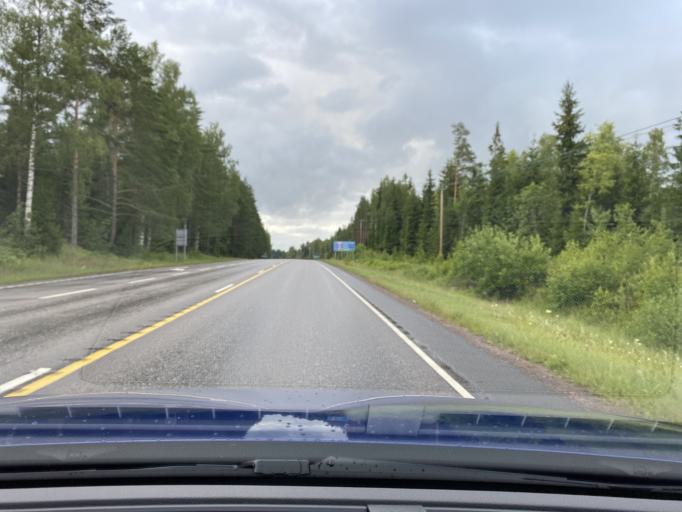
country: FI
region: Uusimaa
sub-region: Helsinki
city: Hyvinge
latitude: 60.5587
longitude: 24.8200
